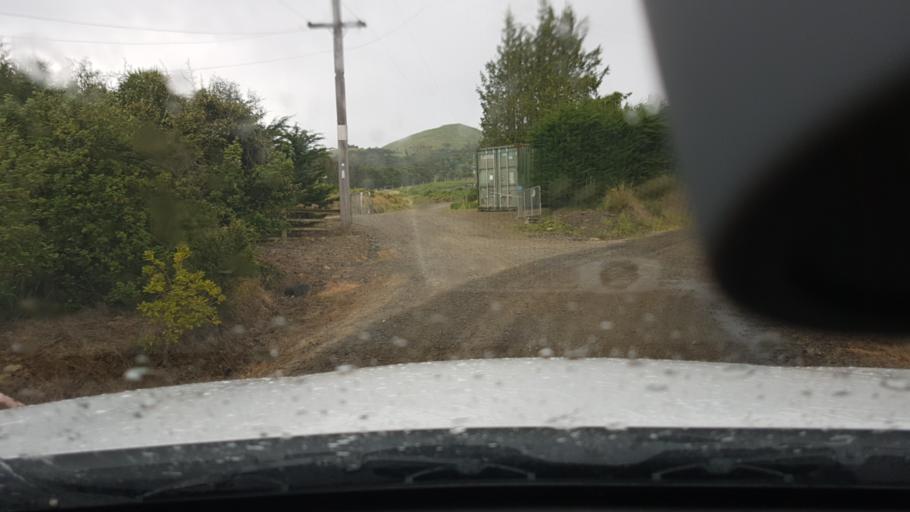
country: NZ
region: Otago
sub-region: Dunedin City
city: Dunedin
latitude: -45.9280
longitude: 170.3474
